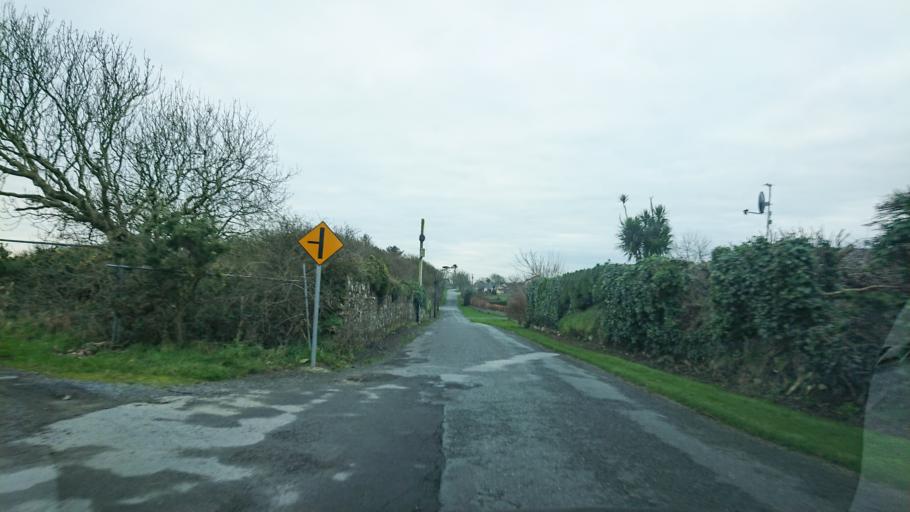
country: IE
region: Munster
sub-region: Waterford
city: Tra Mhor
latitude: 52.1463
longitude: -7.1725
